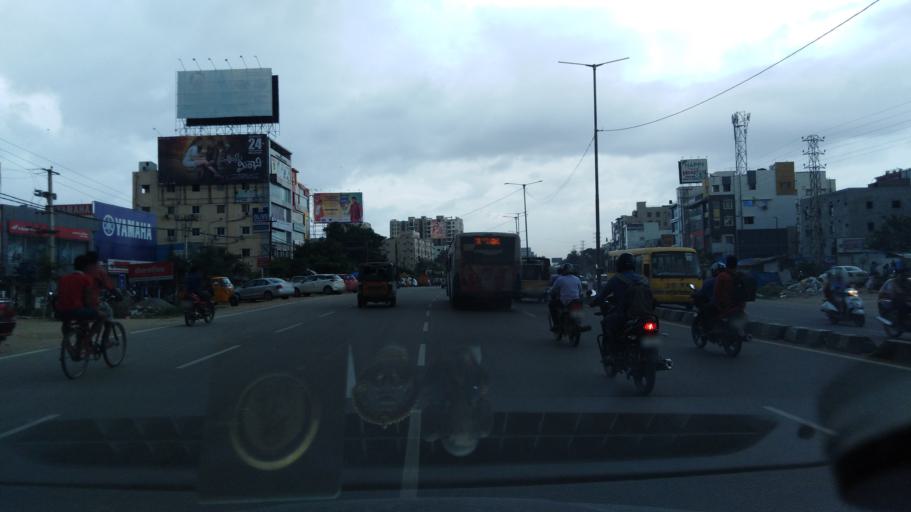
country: IN
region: Telangana
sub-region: Medak
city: Serilingampalle
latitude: 17.4953
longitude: 78.3416
